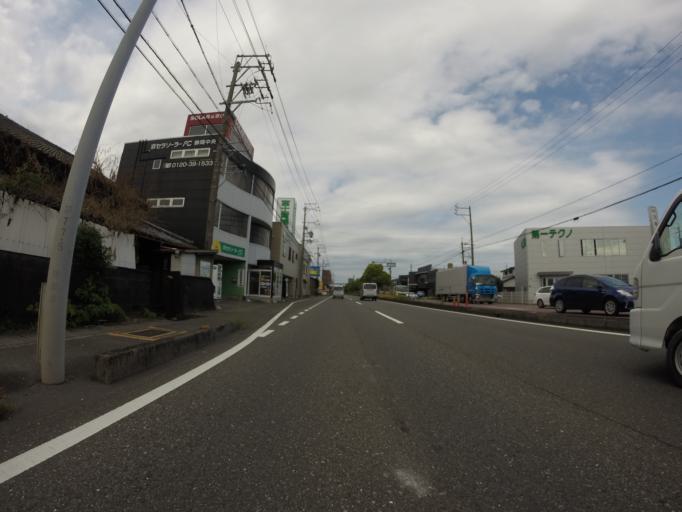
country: JP
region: Shizuoka
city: Shizuoka-shi
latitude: 34.9920
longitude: 138.4199
